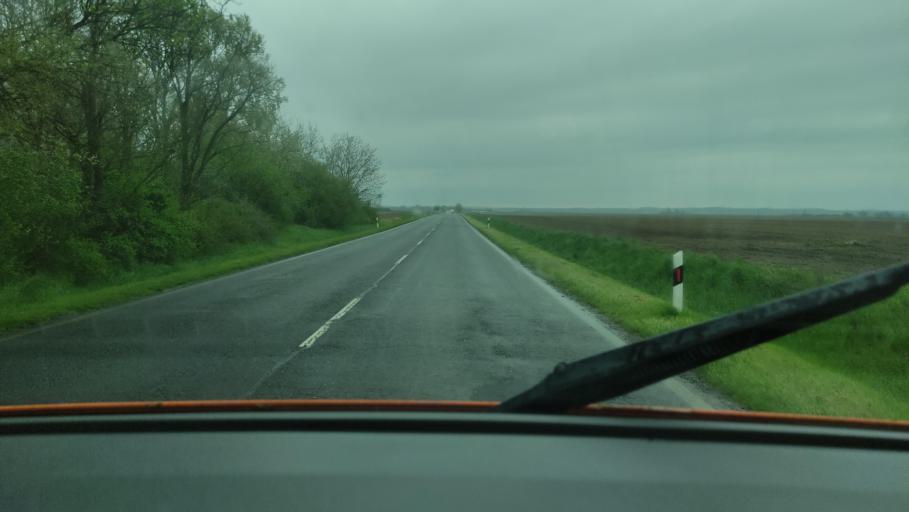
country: HU
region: Baranya
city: Mohacs
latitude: 45.9228
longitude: 18.6595
